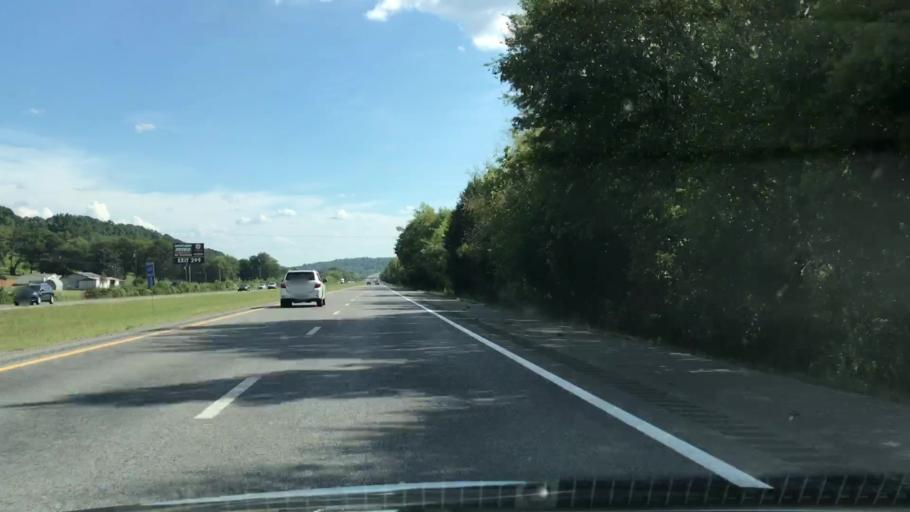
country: US
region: Tennessee
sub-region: Giles County
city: Pulaski
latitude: 35.1543
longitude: -86.8796
